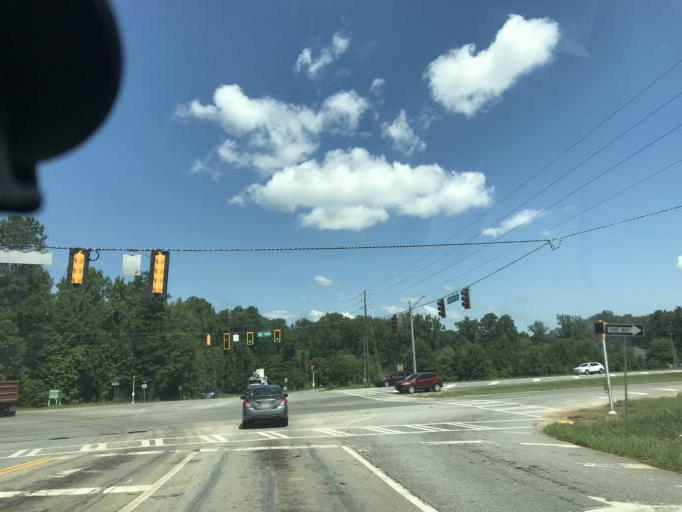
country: US
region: Georgia
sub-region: Forsyth County
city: Cumming
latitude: 34.2710
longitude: -84.0789
